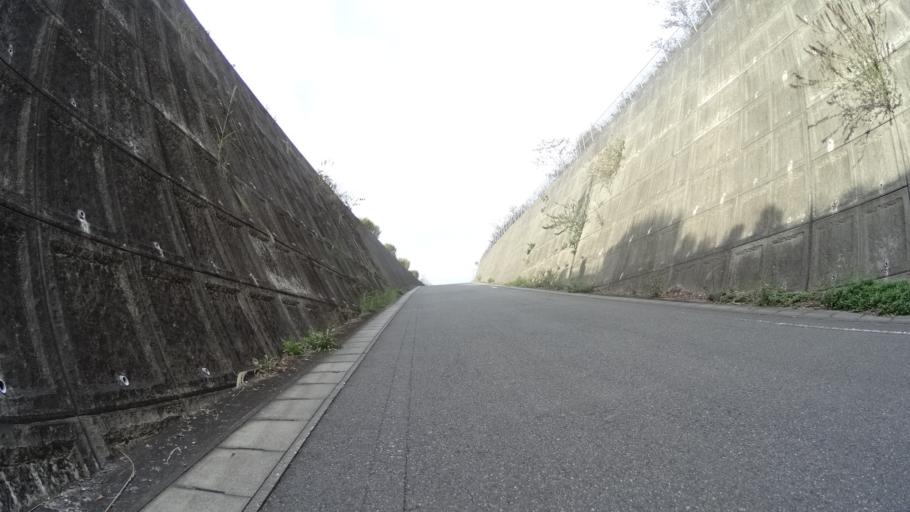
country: JP
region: Yamanashi
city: Otsuki
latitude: 35.6107
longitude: 139.0124
